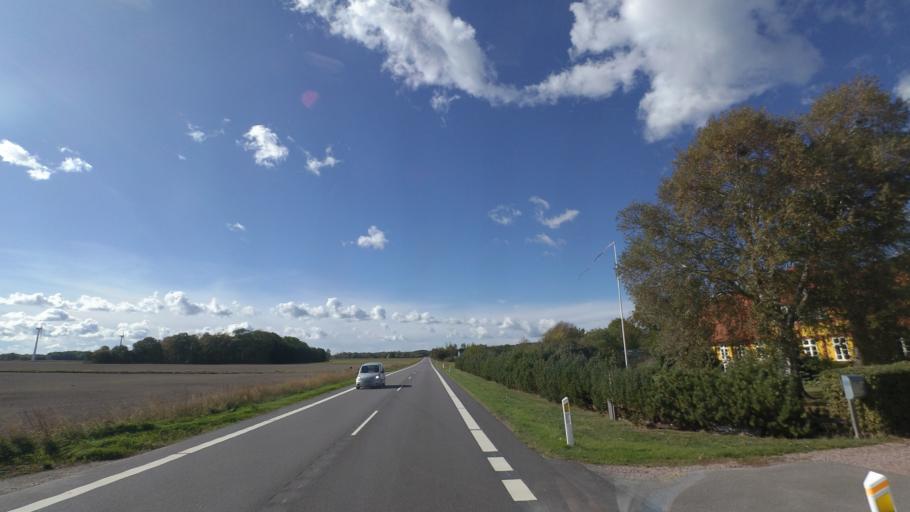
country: DK
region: Capital Region
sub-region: Bornholm Kommune
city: Nexo
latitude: 55.0611
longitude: 15.0629
